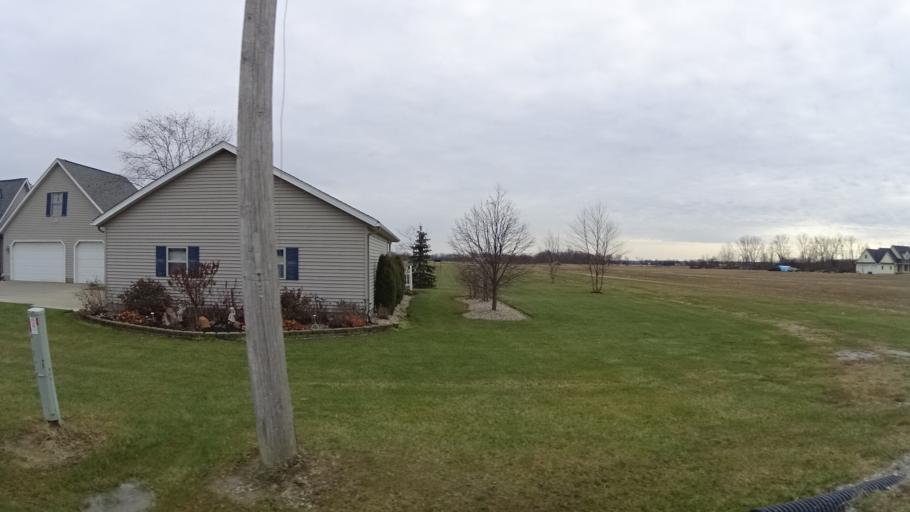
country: US
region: Ohio
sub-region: Lorain County
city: Wellington
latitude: 41.1438
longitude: -82.1818
